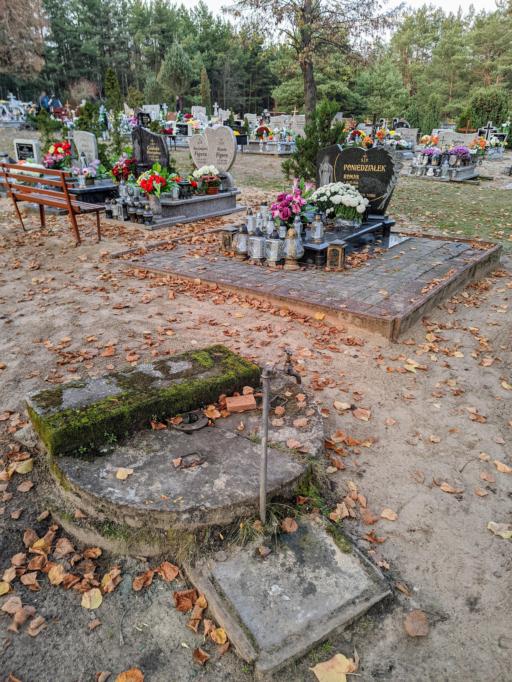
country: PL
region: Lubusz
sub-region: Powiat zielonogorski
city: Bojadla
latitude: 51.9589
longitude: 15.8203
